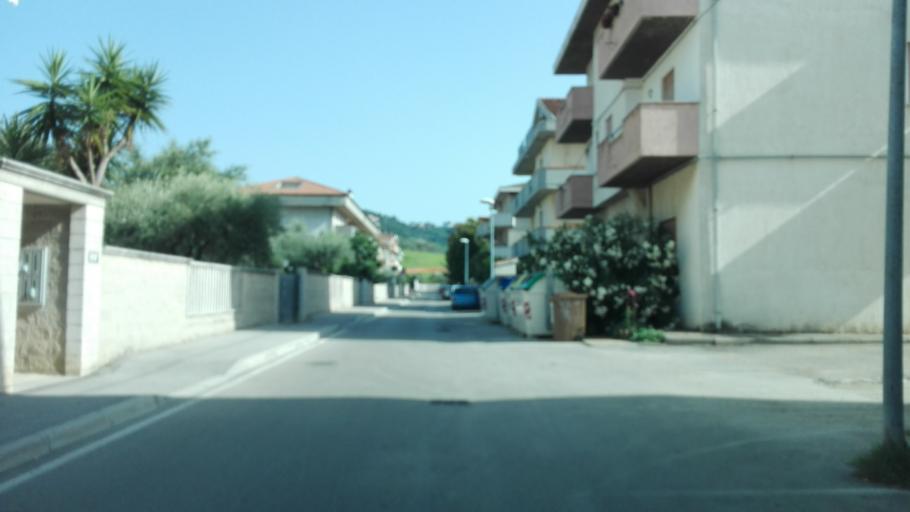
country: IT
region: Abruzzo
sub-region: Provincia di Pescara
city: Montesilvano Marina
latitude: 42.5112
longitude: 14.1479
